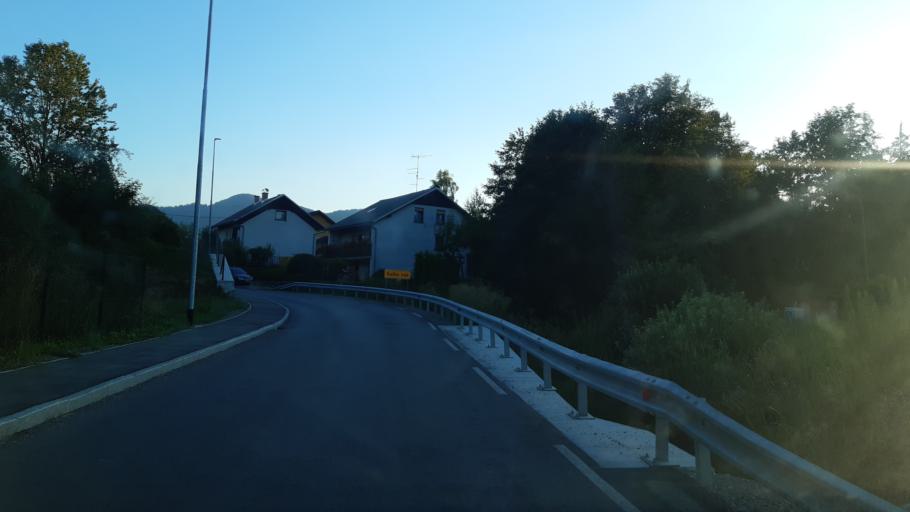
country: SI
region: Kocevje
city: Kocevje
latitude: 45.6547
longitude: 14.8818
